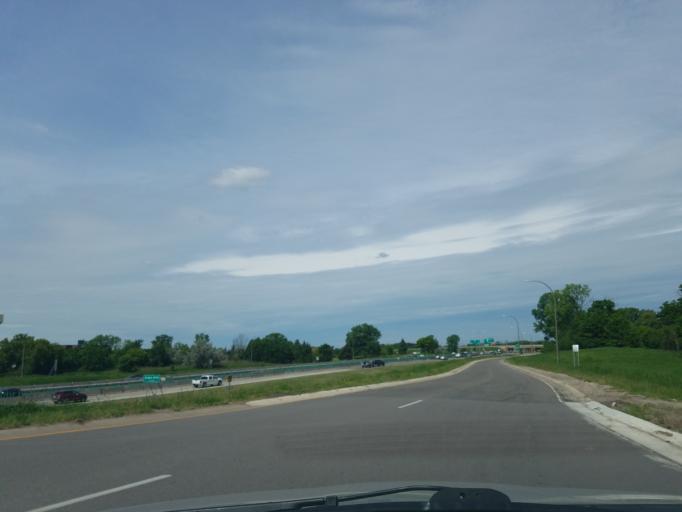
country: US
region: Minnesota
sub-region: Ramsey County
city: Arden Hills
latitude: 45.0606
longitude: -93.1475
